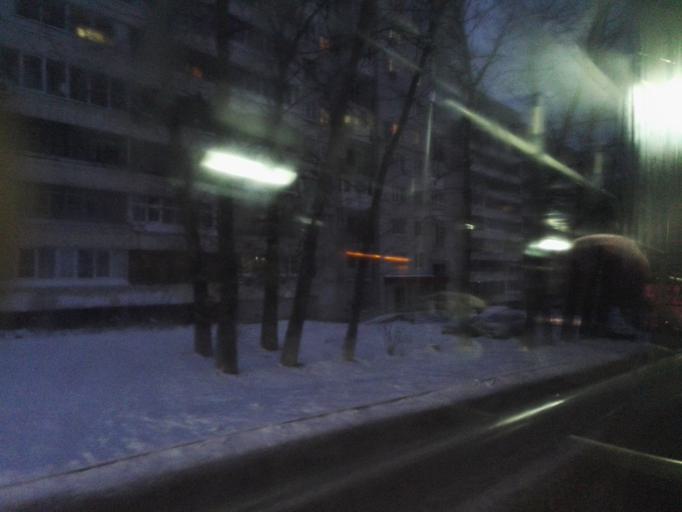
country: RU
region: Tula
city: Mendeleyevskiy
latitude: 54.1603
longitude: 37.6010
